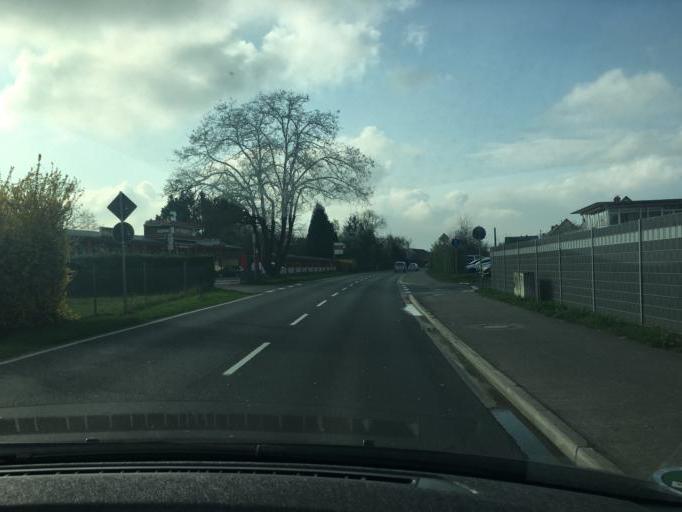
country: DE
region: North Rhine-Westphalia
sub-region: Regierungsbezirk Koln
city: Alfter
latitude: 50.7664
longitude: 7.0494
